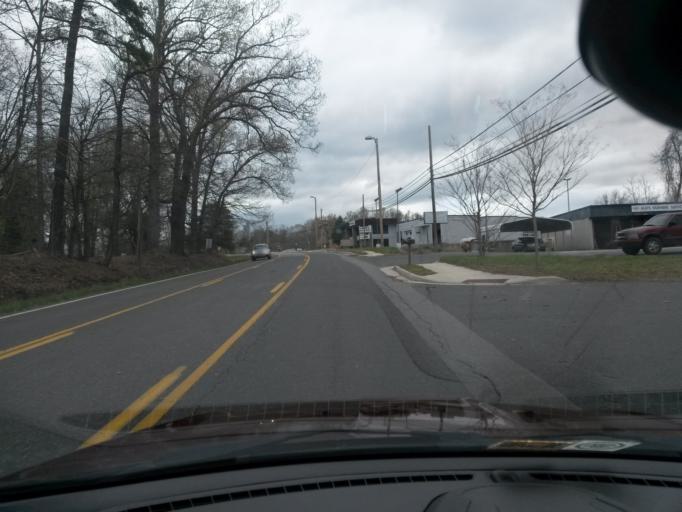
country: US
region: Virginia
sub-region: Amherst County
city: Amherst
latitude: 37.5748
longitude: -79.0576
